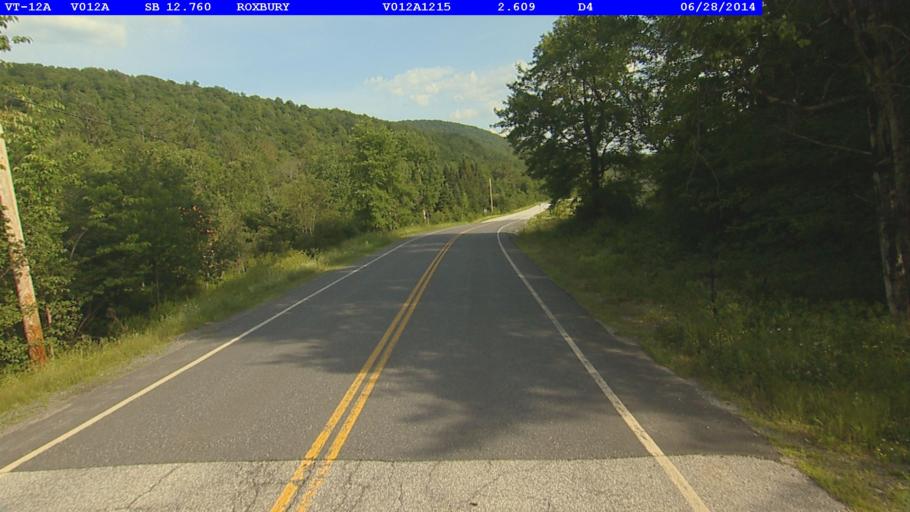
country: US
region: Vermont
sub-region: Washington County
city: Northfield
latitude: 44.0660
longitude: -72.7444
